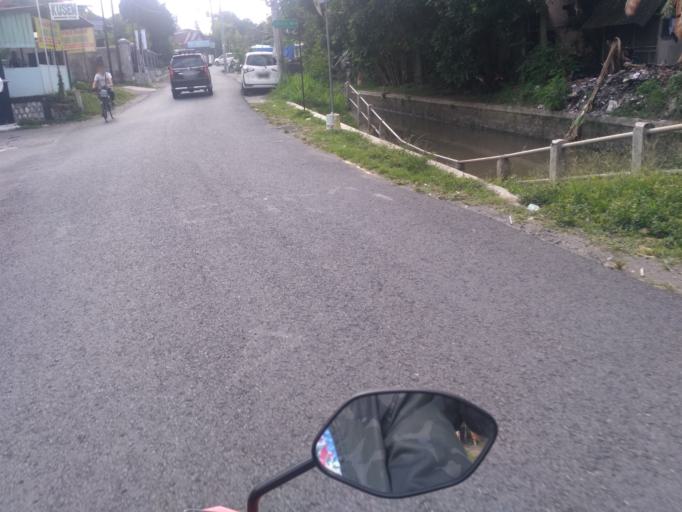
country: ID
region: Daerah Istimewa Yogyakarta
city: Melati
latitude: -7.7586
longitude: 110.3690
